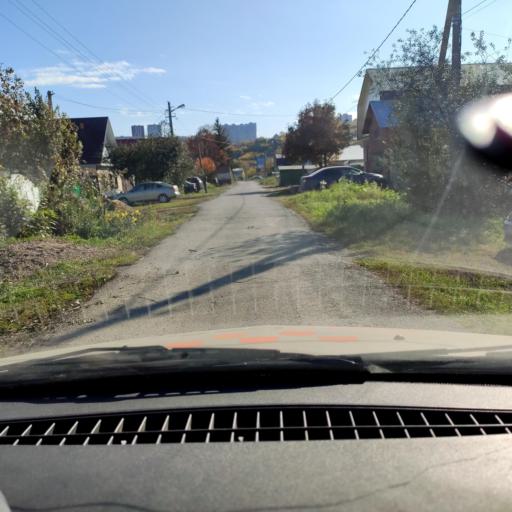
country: RU
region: Bashkortostan
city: Ufa
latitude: 54.7397
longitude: 55.9147
